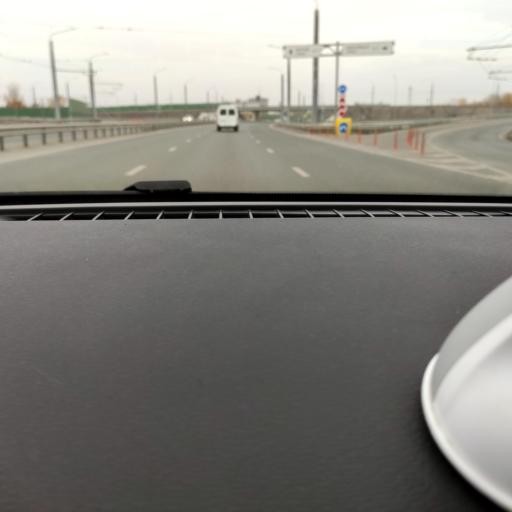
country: RU
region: Samara
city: Samara
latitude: 53.1629
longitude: 50.0875
